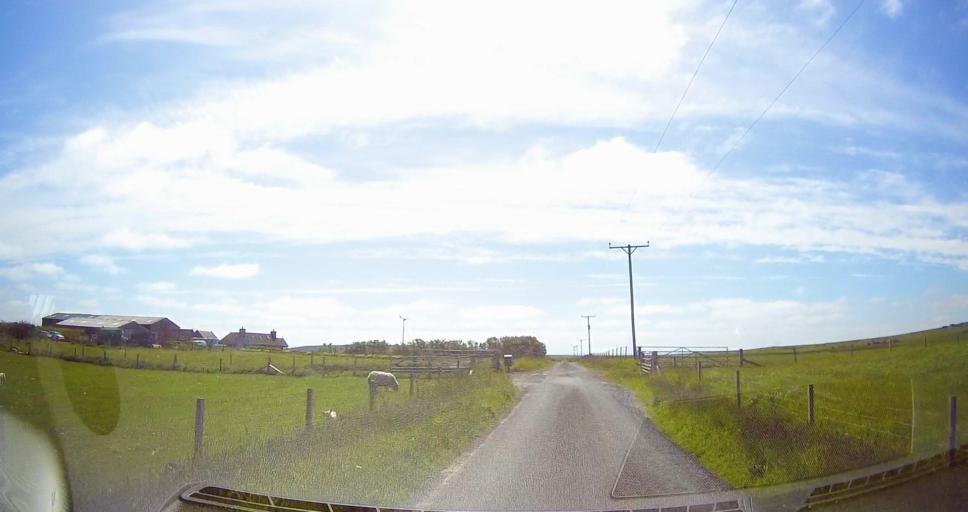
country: GB
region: Scotland
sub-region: Orkney Islands
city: Kirkwall
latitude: 58.8307
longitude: -2.8979
